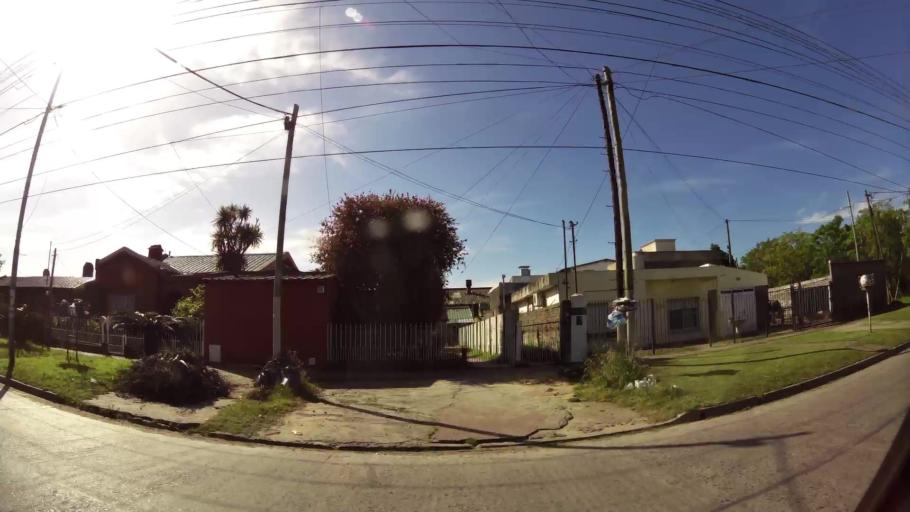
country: AR
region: Buenos Aires
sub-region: Partido de Quilmes
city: Quilmes
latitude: -34.7957
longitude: -58.2292
